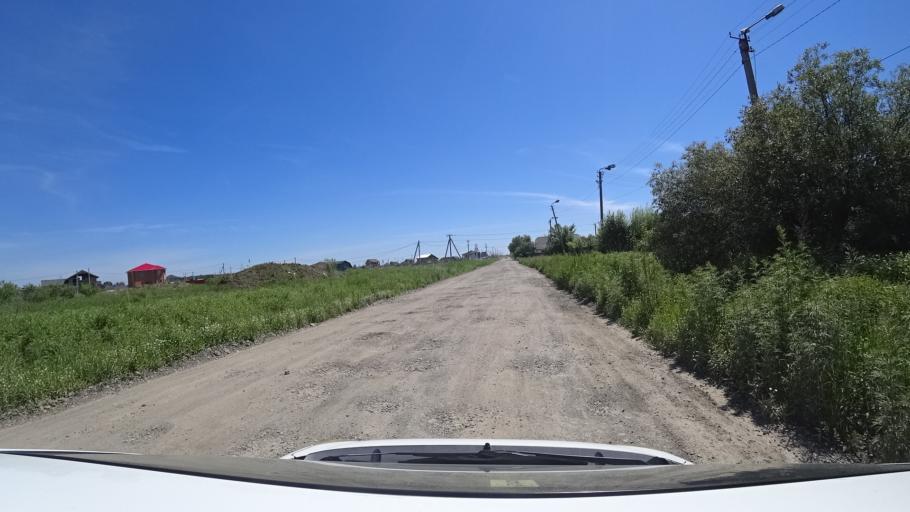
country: RU
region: Khabarovsk Krai
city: Topolevo
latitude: 48.5115
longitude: 135.1918
